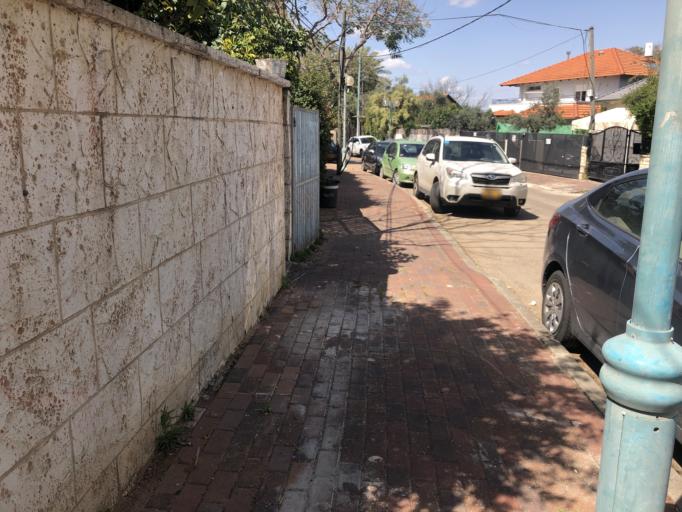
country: IL
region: Central District
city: Kfar Saba
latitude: 32.1607
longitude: 34.9227
